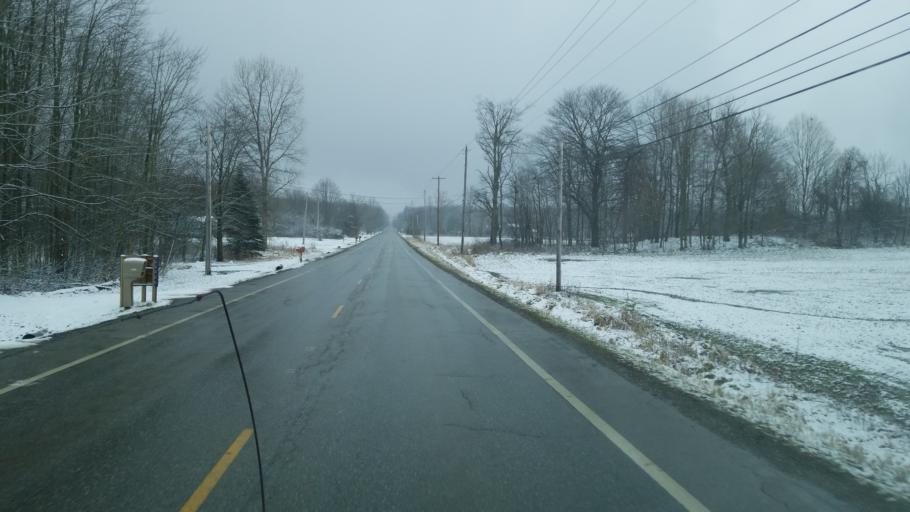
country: US
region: Ohio
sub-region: Portage County
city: Hiram
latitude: 41.3100
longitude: -81.1652
